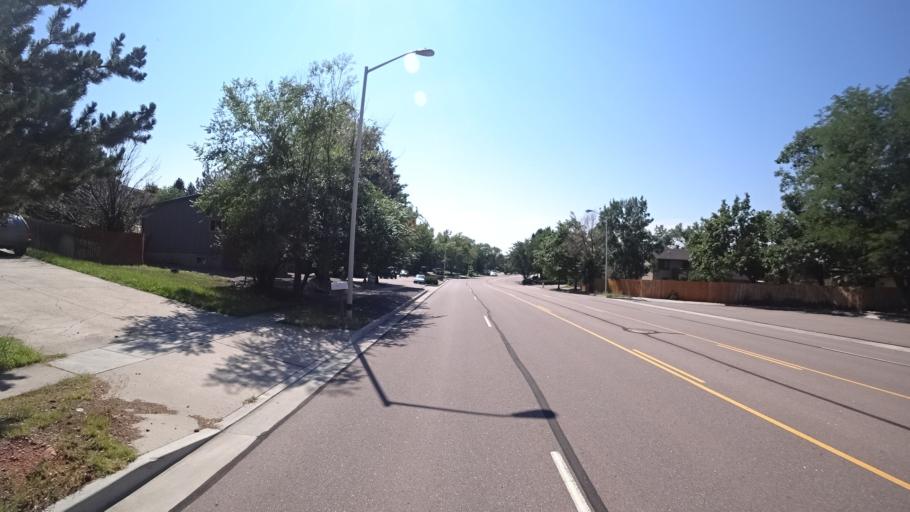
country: US
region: Colorado
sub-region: El Paso County
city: Air Force Academy
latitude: 38.9250
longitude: -104.8284
